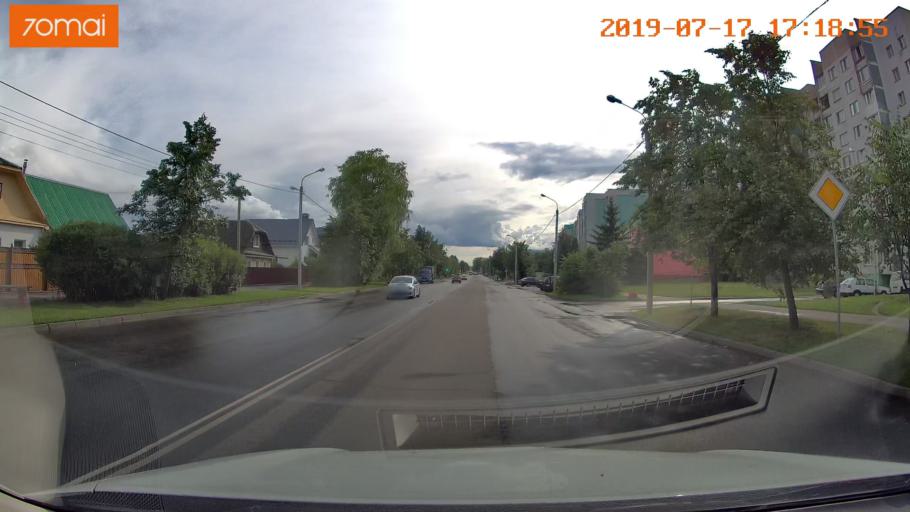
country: BY
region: Mogilev
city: Babruysk
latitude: 53.1592
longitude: 29.1967
